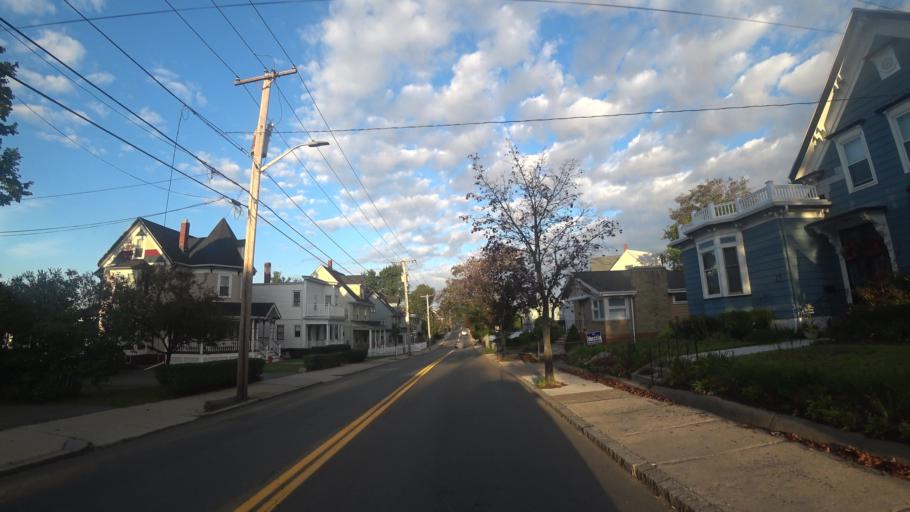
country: US
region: Massachusetts
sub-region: Suffolk County
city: Winthrop
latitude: 42.3724
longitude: -70.9814
